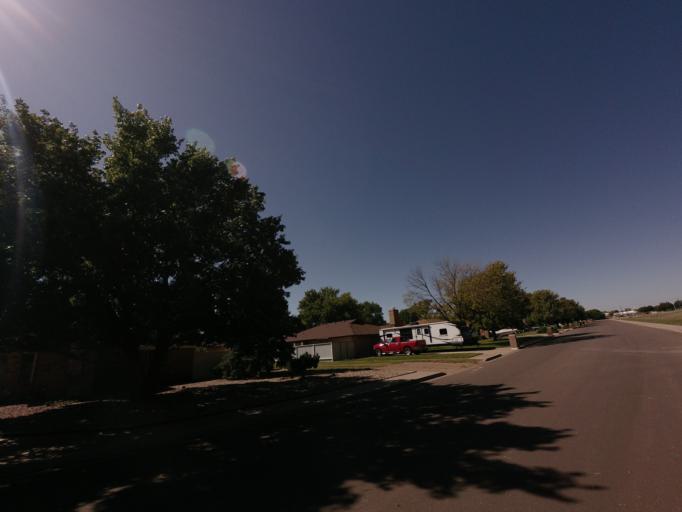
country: US
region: New Mexico
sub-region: Curry County
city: Clovis
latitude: 34.4232
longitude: -103.1747
